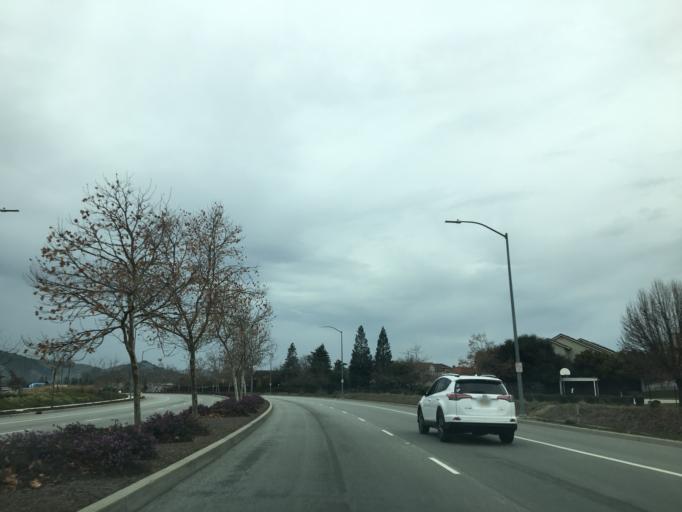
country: US
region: California
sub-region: Santa Clara County
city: Morgan Hill
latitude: 37.1219
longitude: -121.6359
